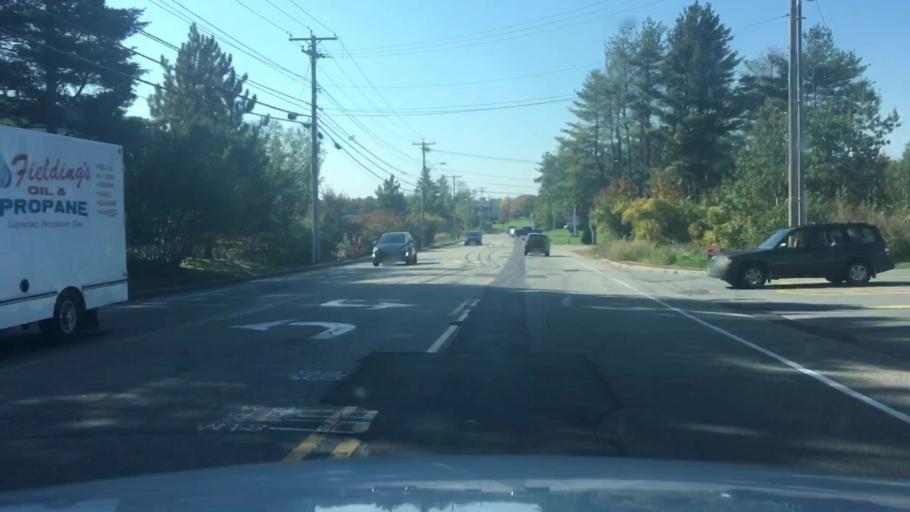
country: US
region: Maine
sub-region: Cumberland County
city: South Portland Gardens
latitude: 43.6505
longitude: -70.3454
